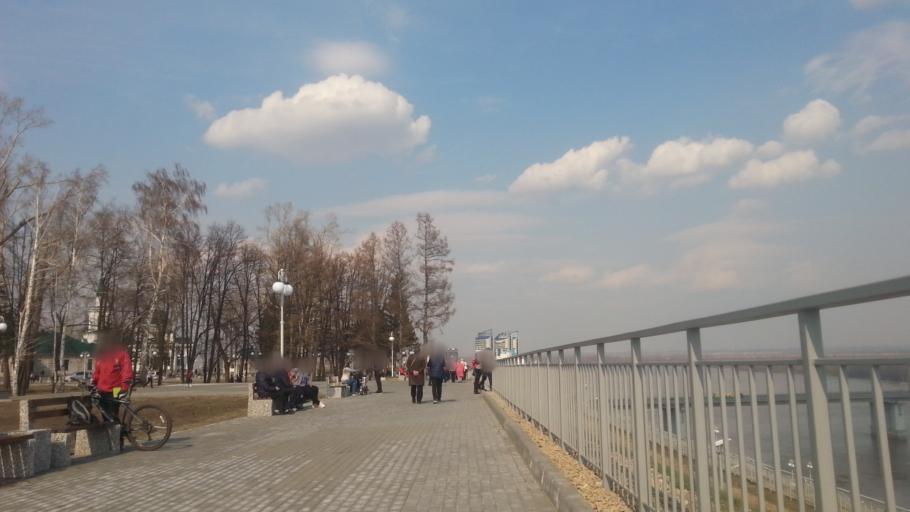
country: RU
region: Altai Krai
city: Zaton
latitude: 53.3218
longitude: 83.7951
